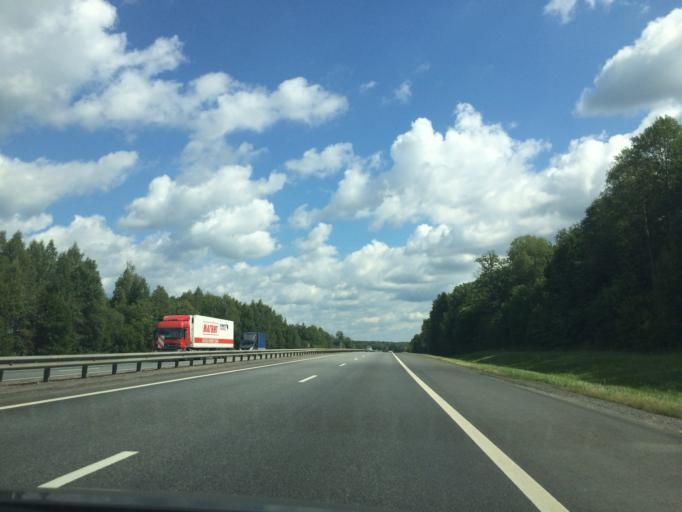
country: RU
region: Vladimir
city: Arsaki
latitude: 56.5102
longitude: 38.5211
